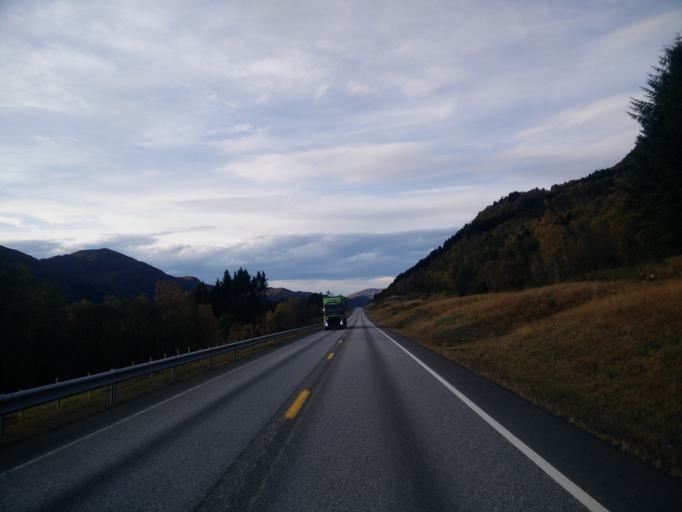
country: NO
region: More og Romsdal
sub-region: Gjemnes
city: Batnfjordsora
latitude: 62.9227
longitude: 7.7023
